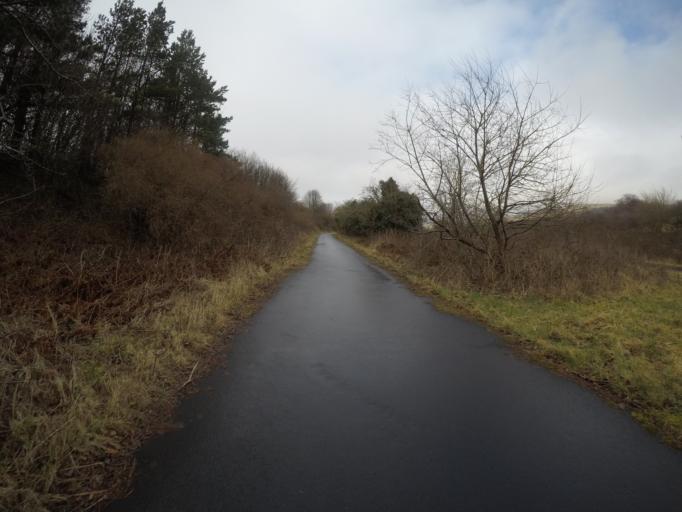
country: GB
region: Scotland
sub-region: North Ayrshire
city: Fairlie
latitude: 55.7324
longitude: -4.8639
